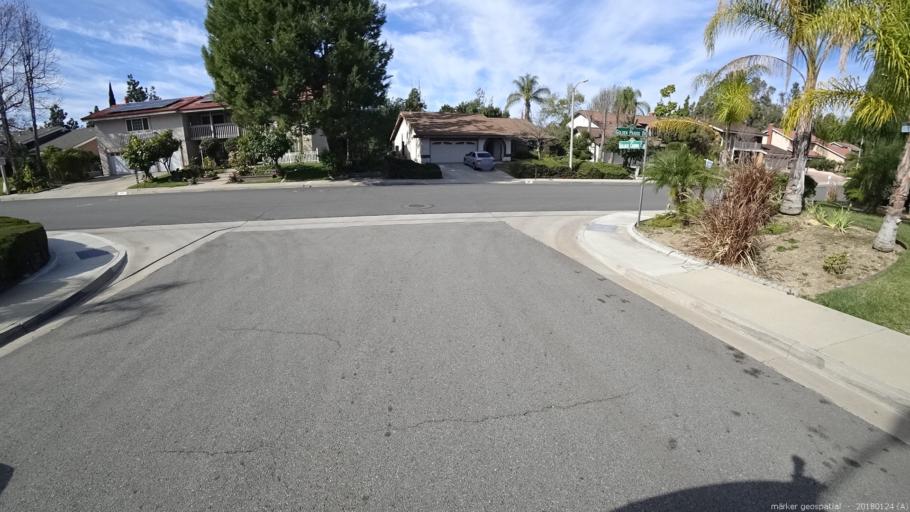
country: US
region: California
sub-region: Los Angeles County
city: Diamond Bar
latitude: 34.0148
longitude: -117.8143
